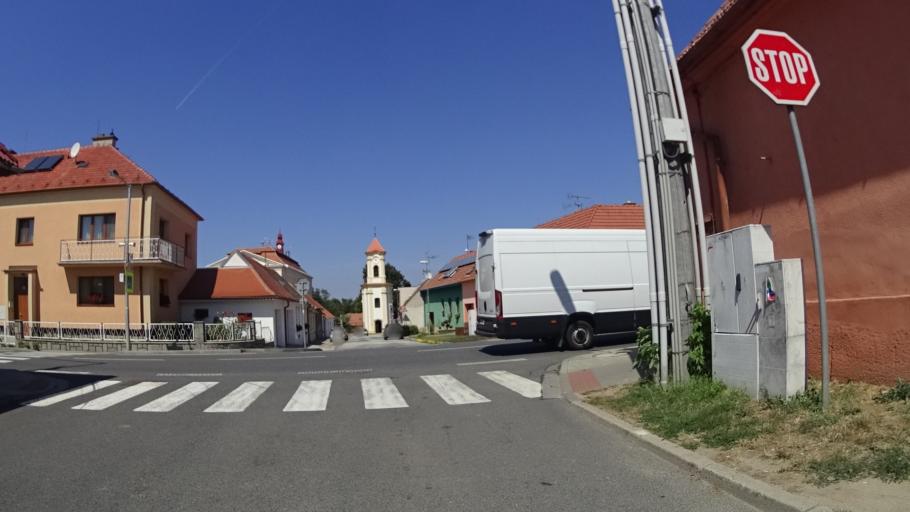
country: CZ
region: South Moravian
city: Straznice
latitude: 48.8973
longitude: 17.3080
